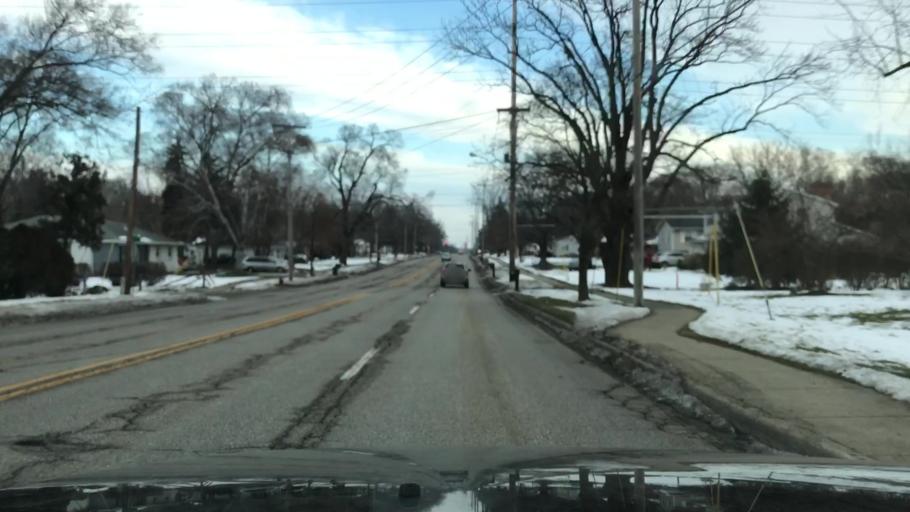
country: US
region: Michigan
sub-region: Kent County
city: Grandville
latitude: 42.9023
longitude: -85.7438
